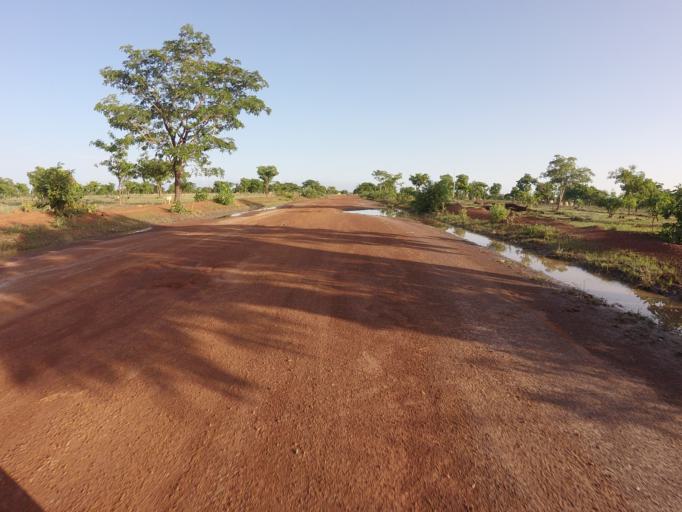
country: TG
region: Savanes
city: Sansanne-Mango
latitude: 10.3618
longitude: -0.0936
